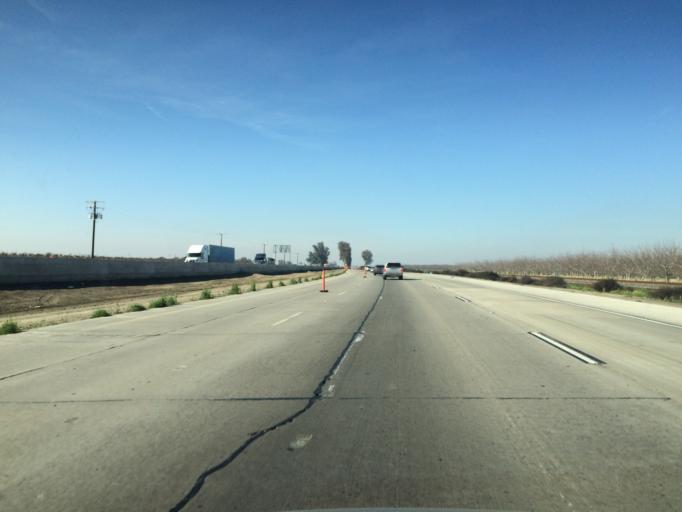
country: US
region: California
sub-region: Tulare County
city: Goshen
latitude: 36.3641
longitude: -119.4298
